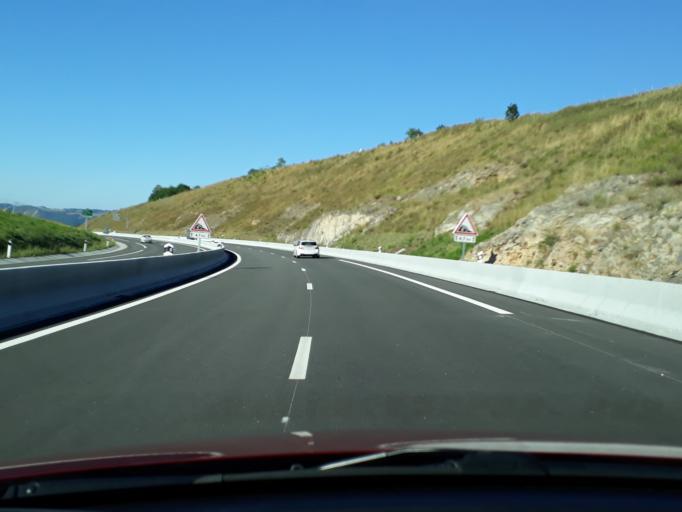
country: FR
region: Auvergne
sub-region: Departement de la Haute-Loire
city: Vals-pres-le-Puy
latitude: 45.0197
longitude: 3.9004
